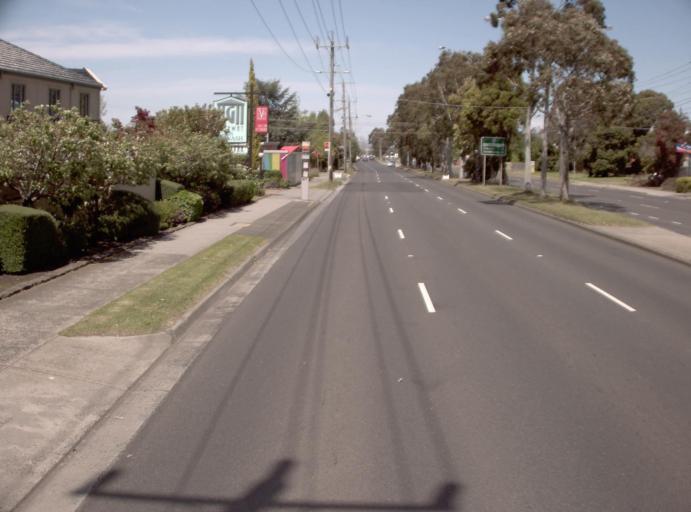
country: AU
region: Victoria
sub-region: Monash
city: Notting Hill
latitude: -37.9018
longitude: 145.1430
